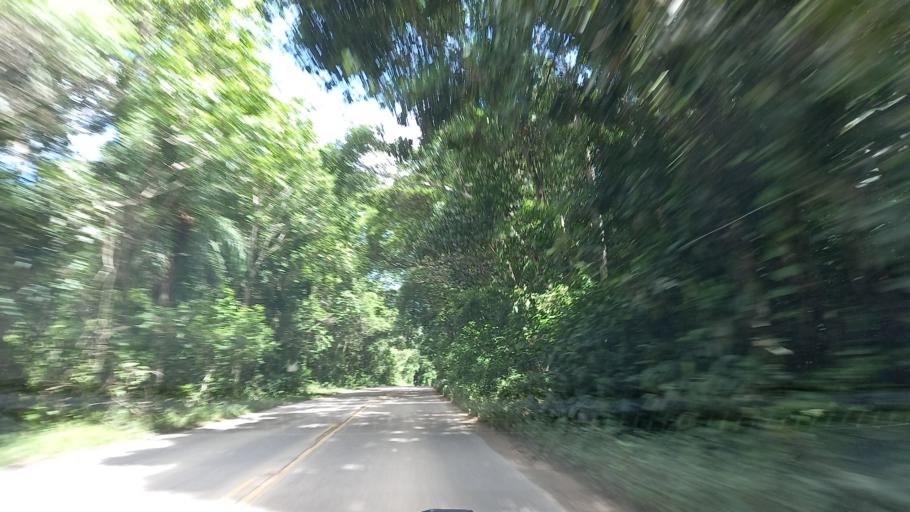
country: BR
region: Pernambuco
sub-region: Rio Formoso
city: Rio Formoso
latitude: -8.7278
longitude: -35.1731
